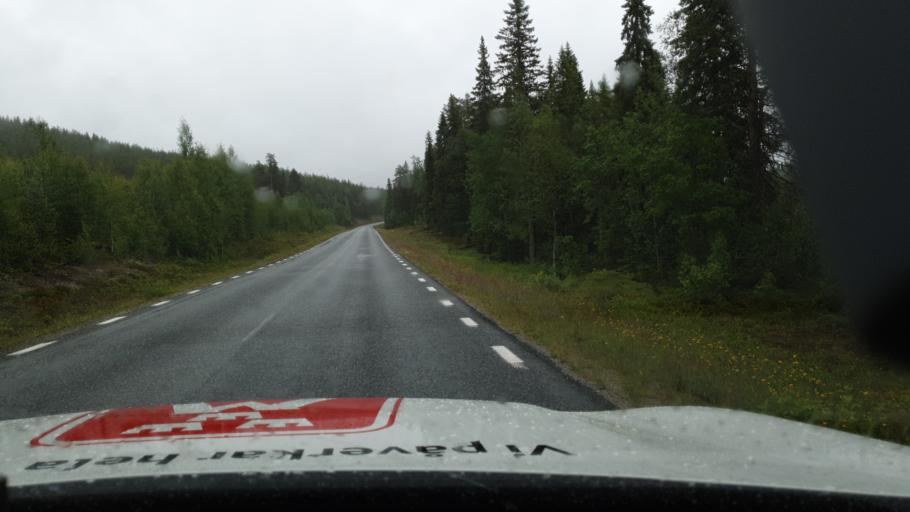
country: SE
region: Vaesterbotten
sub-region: Asele Kommun
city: Insjon
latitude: 64.3501
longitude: 17.8307
